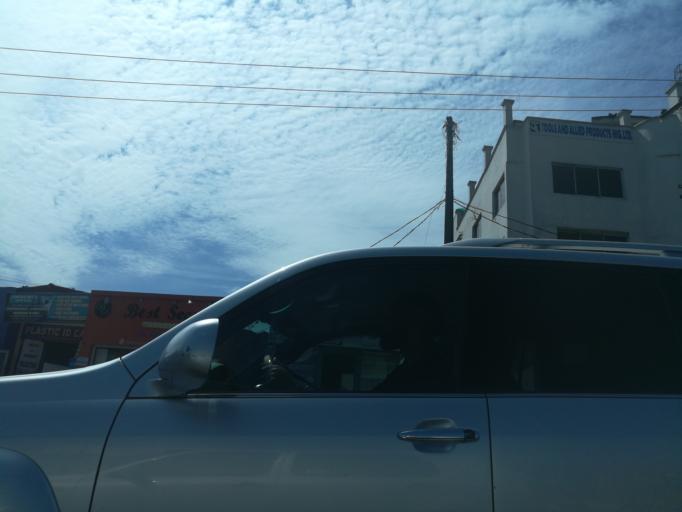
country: NG
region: Lagos
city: Ikeja
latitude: 6.6039
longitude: 3.3460
